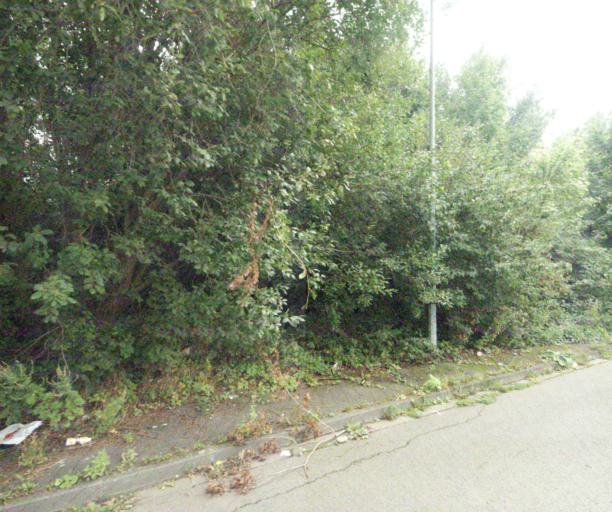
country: FR
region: Nord-Pas-de-Calais
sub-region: Departement du Nord
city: Ronchin
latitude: 50.6173
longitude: 3.0942
